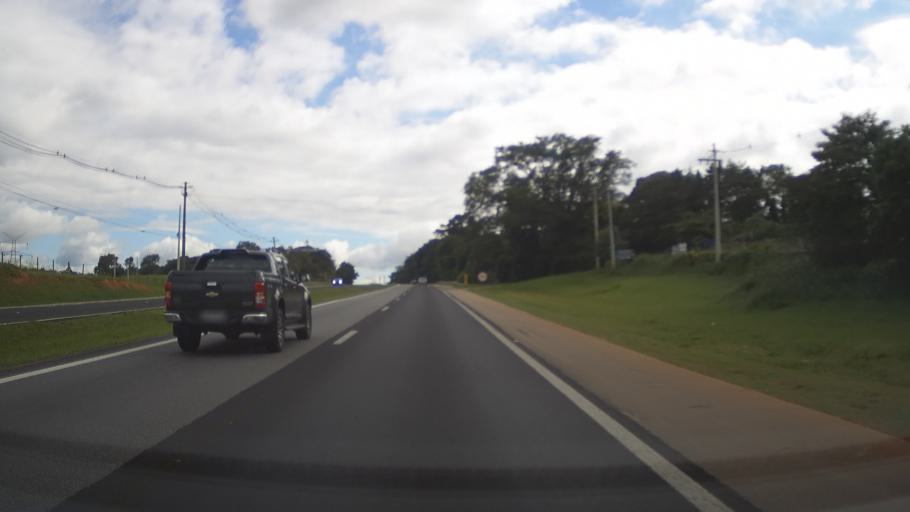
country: BR
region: Sao Paulo
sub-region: Itupeva
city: Itupeva
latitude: -23.2163
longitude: -47.0200
